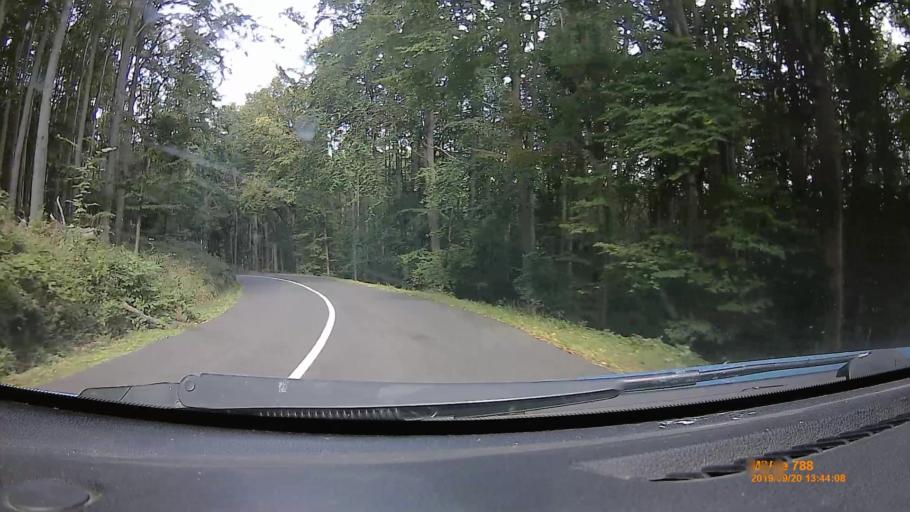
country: HU
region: Borsod-Abauj-Zemplen
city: Saly
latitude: 48.0597
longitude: 20.5592
